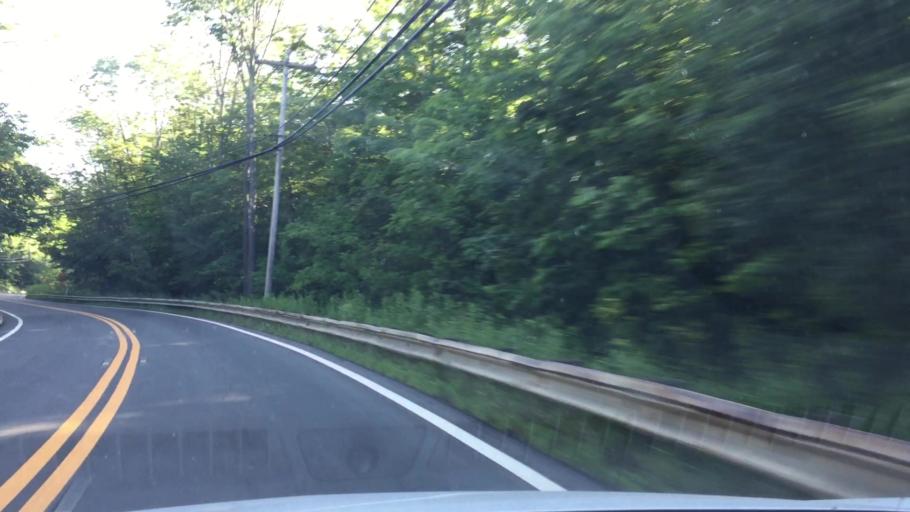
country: US
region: Massachusetts
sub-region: Berkshire County
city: Becket
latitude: 42.3233
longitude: -73.0845
